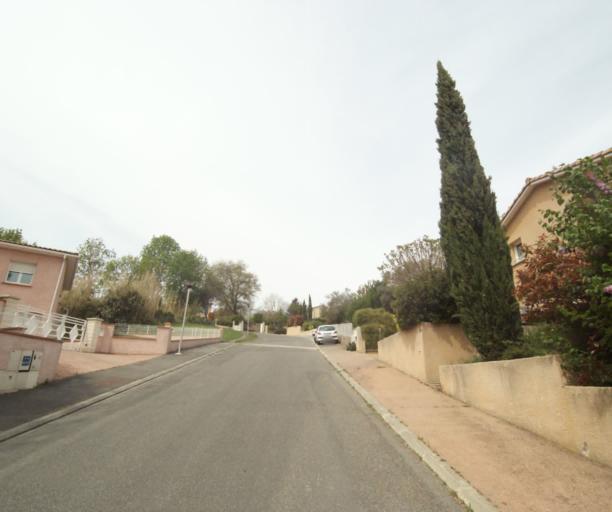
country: FR
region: Midi-Pyrenees
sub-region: Departement de la Haute-Garonne
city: Pechabou
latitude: 43.5039
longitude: 1.5046
